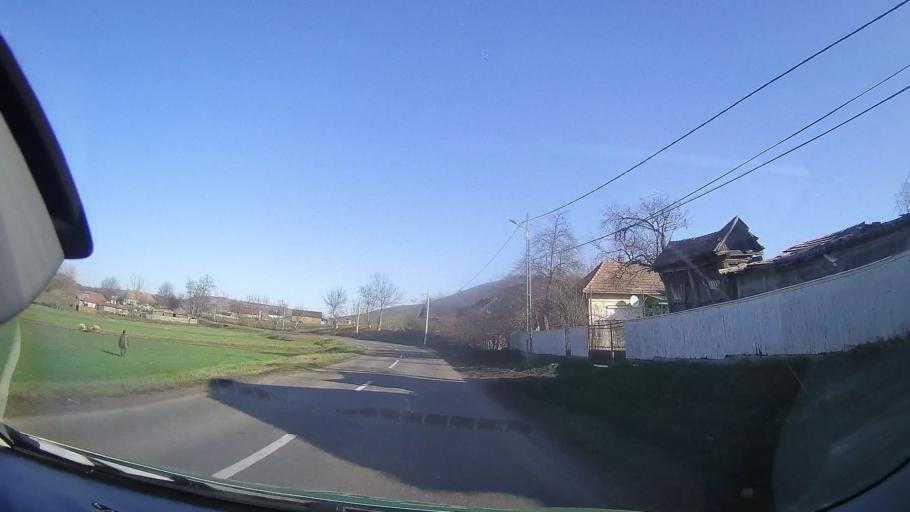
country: RO
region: Mures
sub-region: Comuna Band
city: Band
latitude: 46.5724
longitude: 24.3470
